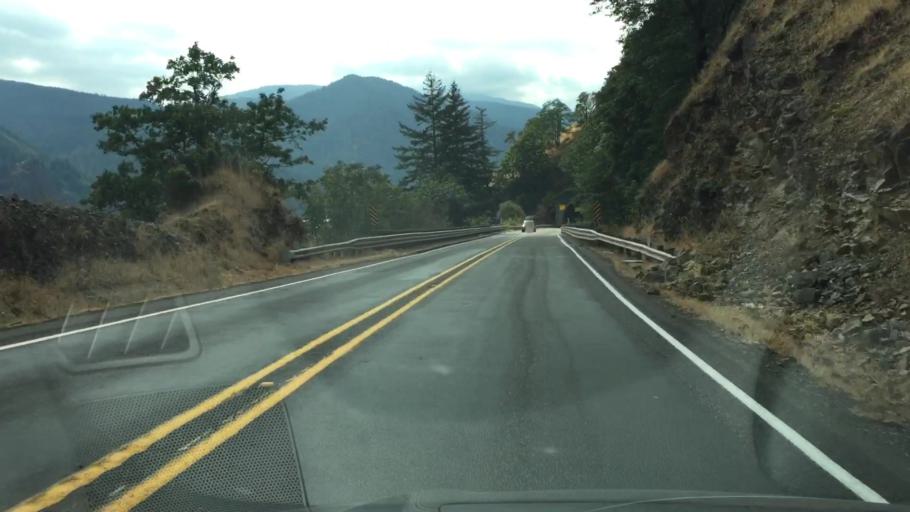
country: US
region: Oregon
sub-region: Hood River County
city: Hood River
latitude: 45.7191
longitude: -121.6076
